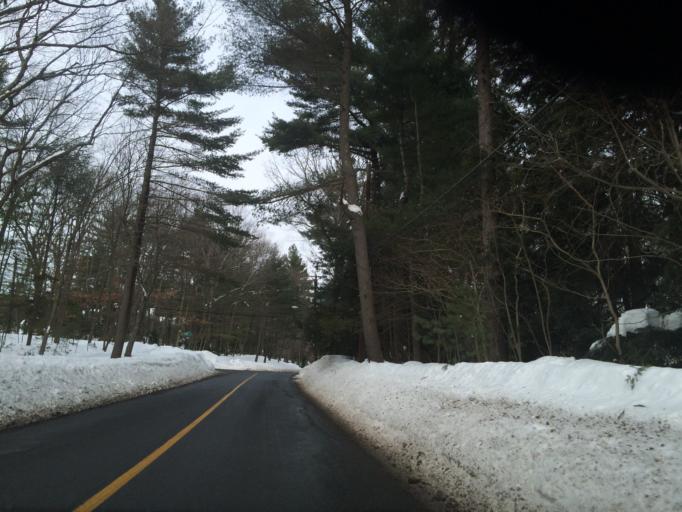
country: US
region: Massachusetts
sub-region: Middlesex County
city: Weston
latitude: 42.3427
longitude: -71.3186
